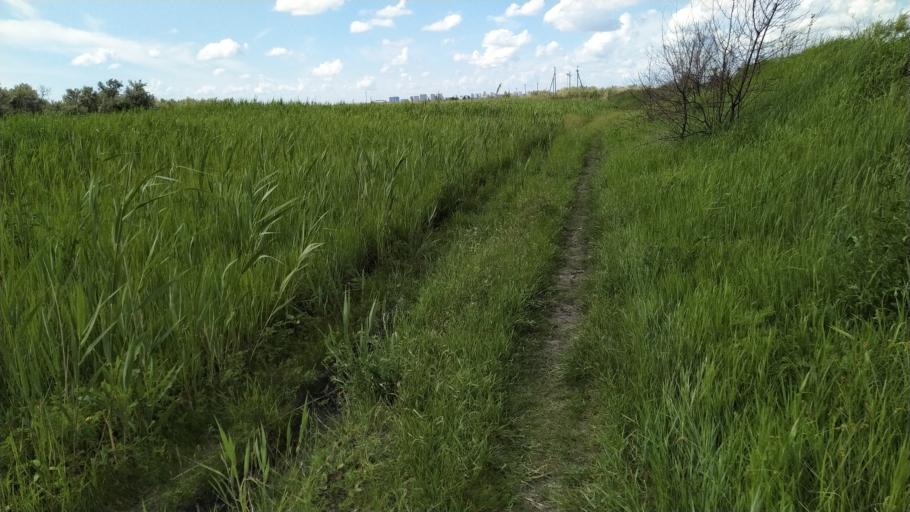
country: RU
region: Rostov
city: Bataysk
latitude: 47.1395
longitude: 39.6694
